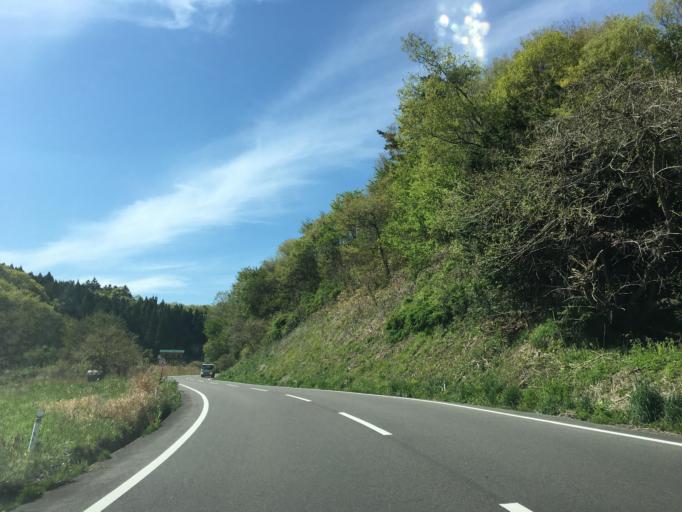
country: JP
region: Fukushima
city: Funehikimachi-funehiki
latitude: 37.3204
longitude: 140.6216
